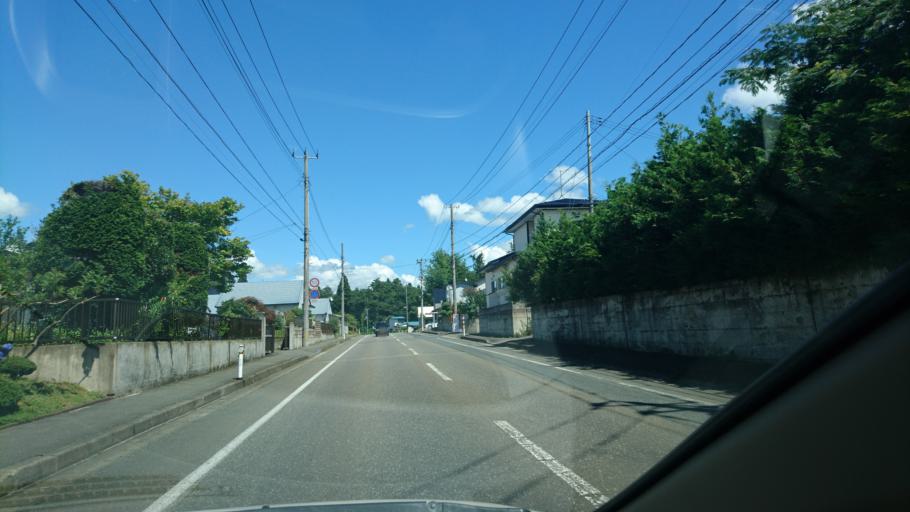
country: JP
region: Iwate
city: Kitakami
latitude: 39.3003
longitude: 141.1303
